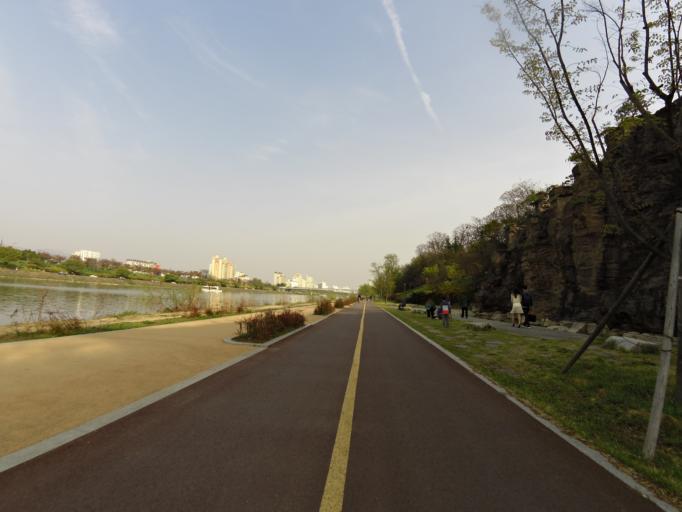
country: KR
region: Daegu
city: Daegu
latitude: 35.8873
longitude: 128.6427
